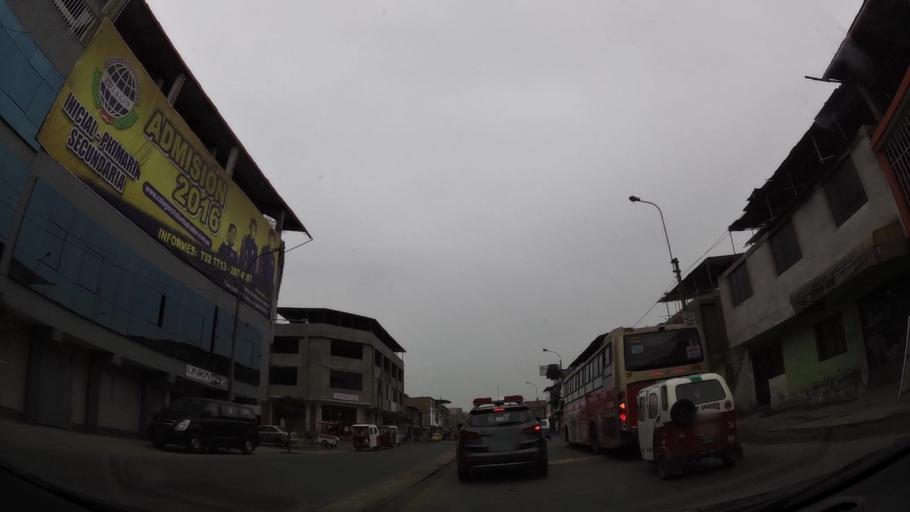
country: PE
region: Lima
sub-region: Lima
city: Surco
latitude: -12.2226
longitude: -76.9312
